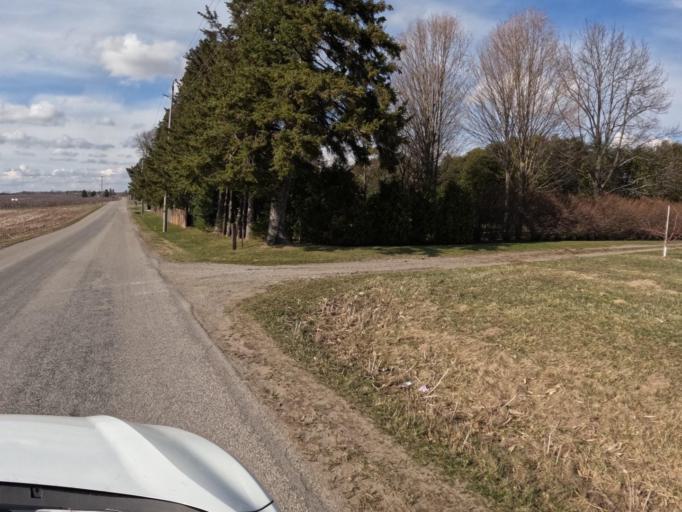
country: CA
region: Ontario
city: Norfolk County
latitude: 42.8679
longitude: -80.2767
